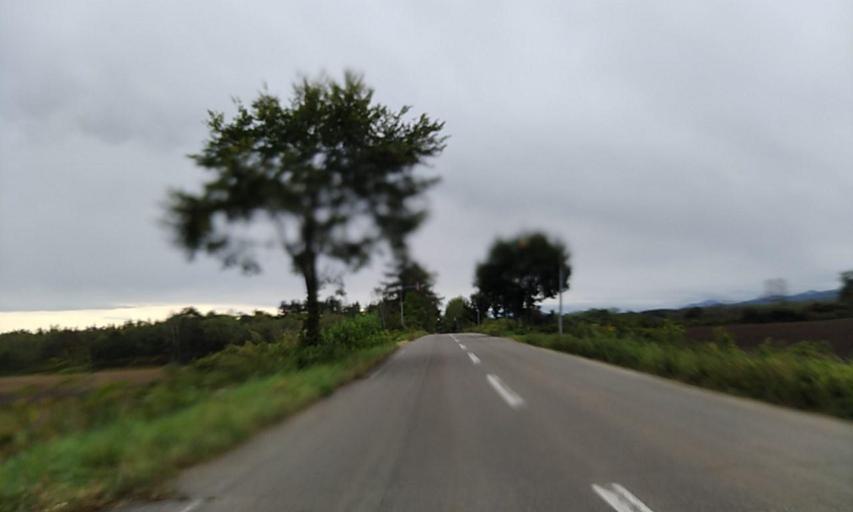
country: JP
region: Hokkaido
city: Obihiro
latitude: 42.6501
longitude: 143.0863
